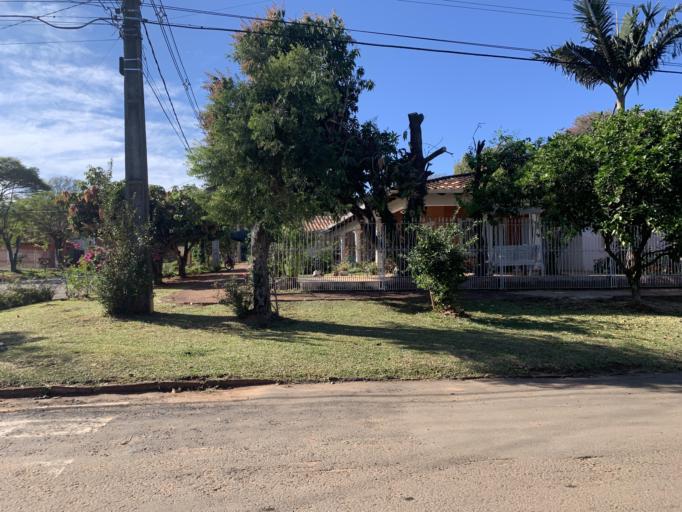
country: PY
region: Misiones
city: San Juan Bautista
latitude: -26.6678
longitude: -57.1370
